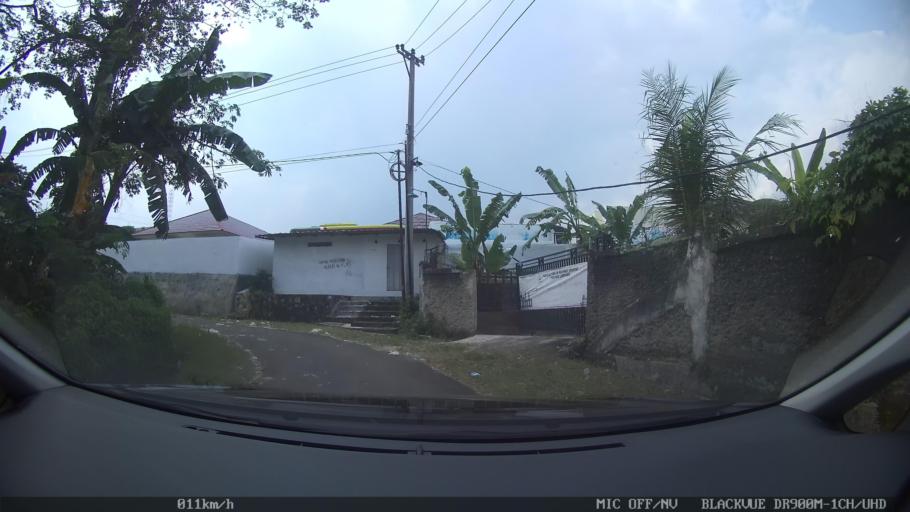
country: ID
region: Lampung
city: Bandarlampung
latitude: -5.4310
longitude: 105.2703
